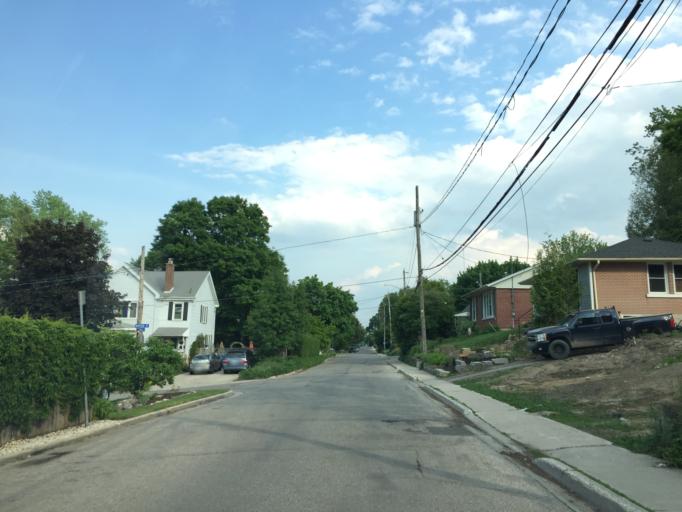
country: CA
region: Ontario
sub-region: Wellington County
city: Guelph
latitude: 43.5543
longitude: -80.2708
